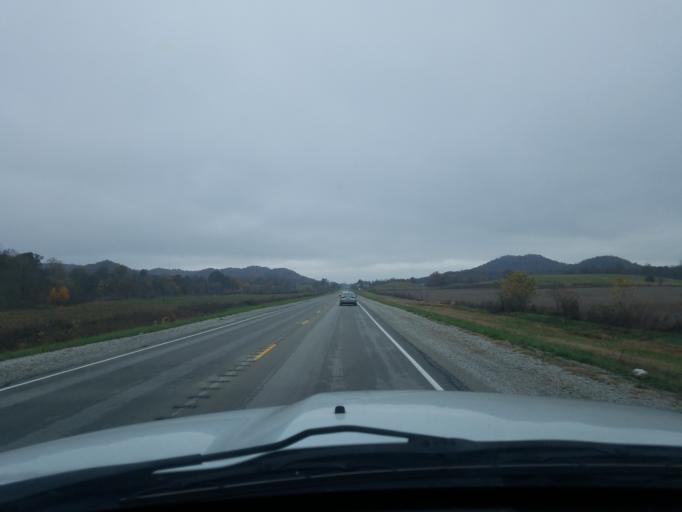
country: US
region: Kentucky
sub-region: Marion County
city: Lebanon
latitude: 37.5101
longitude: -85.2953
